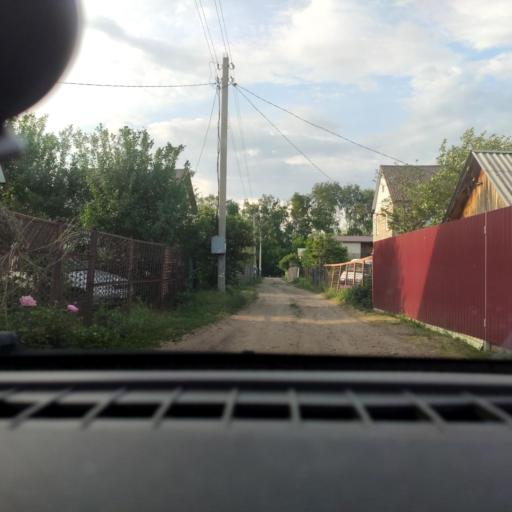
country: RU
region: Samara
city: Tol'yatti
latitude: 53.5963
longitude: 49.3211
